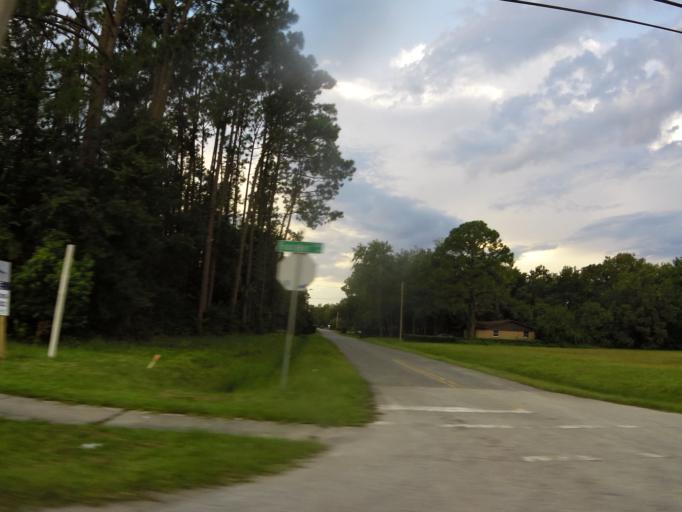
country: US
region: Florida
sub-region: Clay County
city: Bellair-Meadowbrook Terrace
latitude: 30.2869
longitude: -81.7814
